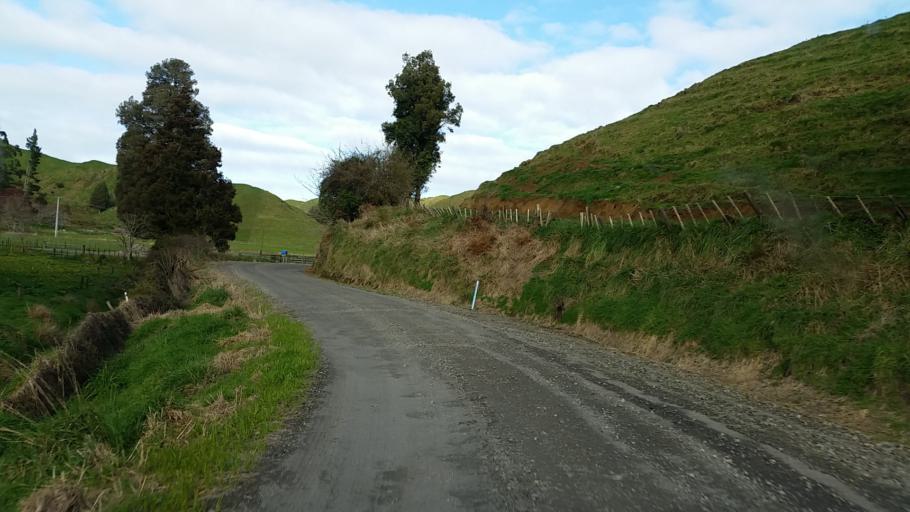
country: NZ
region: Taranaki
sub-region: South Taranaki District
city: Eltham
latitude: -39.2558
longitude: 174.5185
